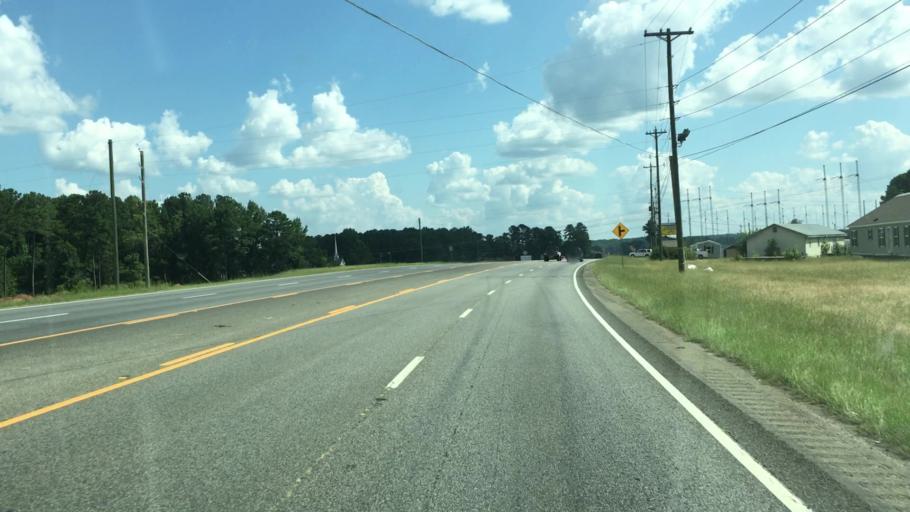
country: US
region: Georgia
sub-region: Baldwin County
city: Milledgeville
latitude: 33.2048
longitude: -83.2963
